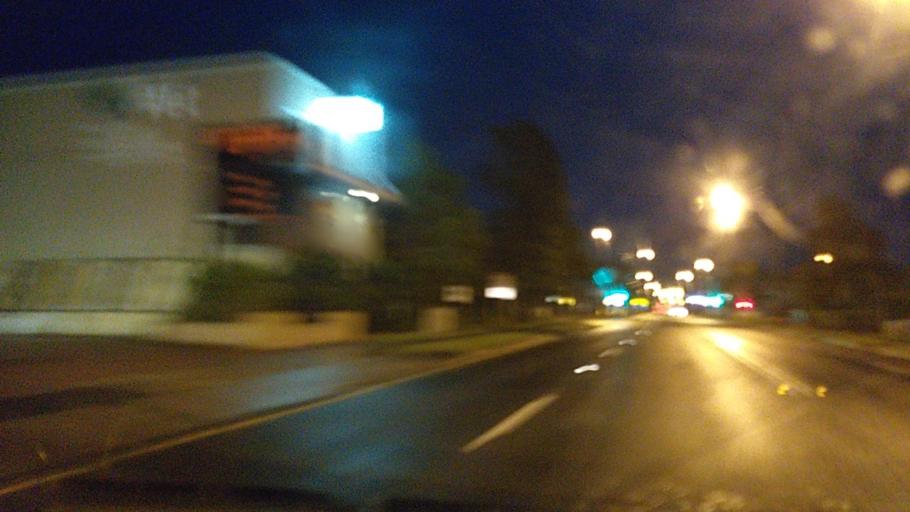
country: AU
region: New South Wales
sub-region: Wollongong
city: Fairy Meadow
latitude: -34.3890
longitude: 150.8938
